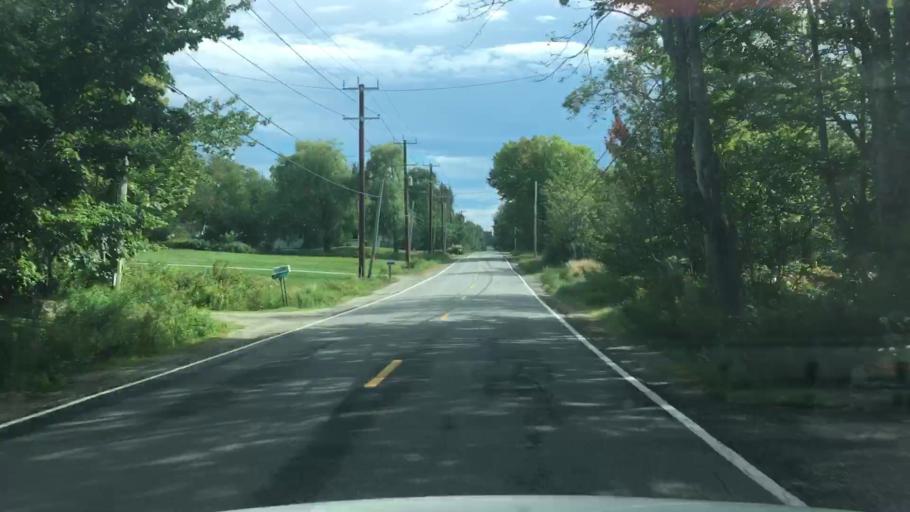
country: US
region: Maine
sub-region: Hancock County
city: Ellsworth
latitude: 44.4974
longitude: -68.4204
